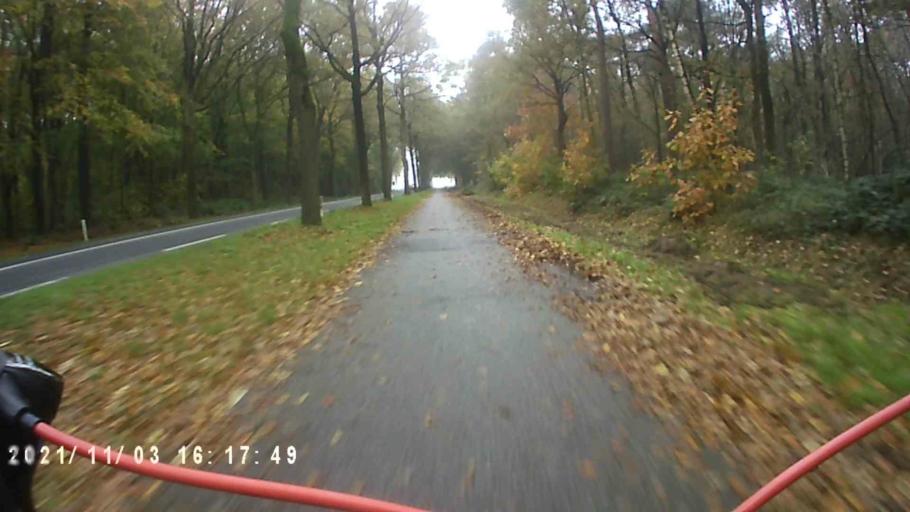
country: NL
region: Groningen
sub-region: Gemeente Leek
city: Leek
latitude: 53.0131
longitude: 6.3228
